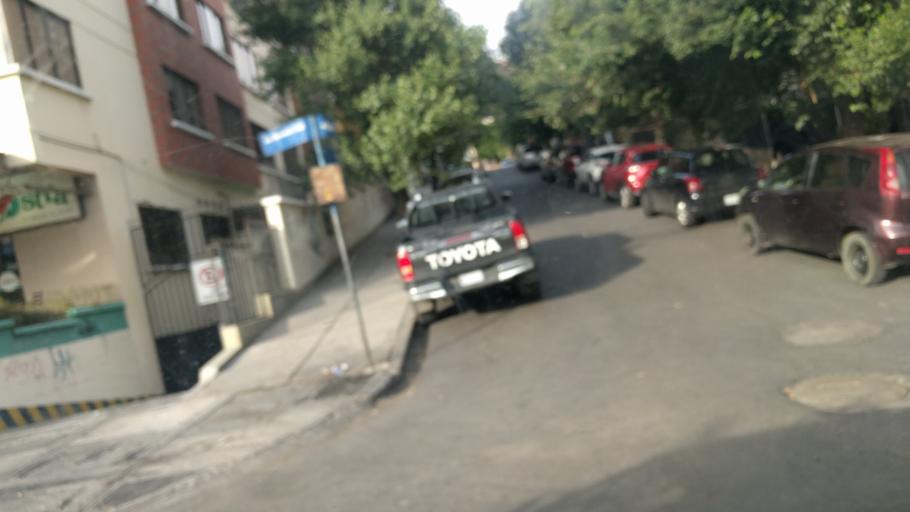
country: BO
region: La Paz
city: La Paz
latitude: -16.5256
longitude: -68.1089
